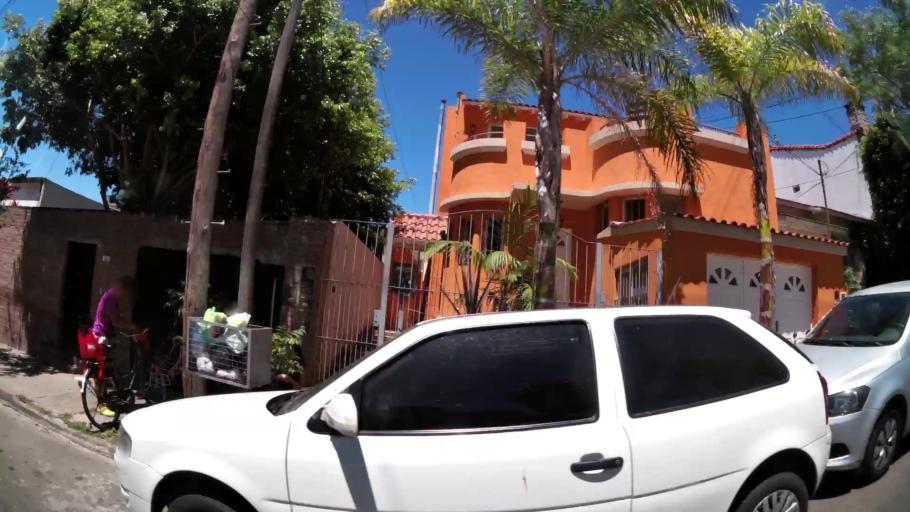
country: AR
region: Buenos Aires
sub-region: Partido de Tigre
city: Tigre
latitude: -34.4437
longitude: -58.5474
